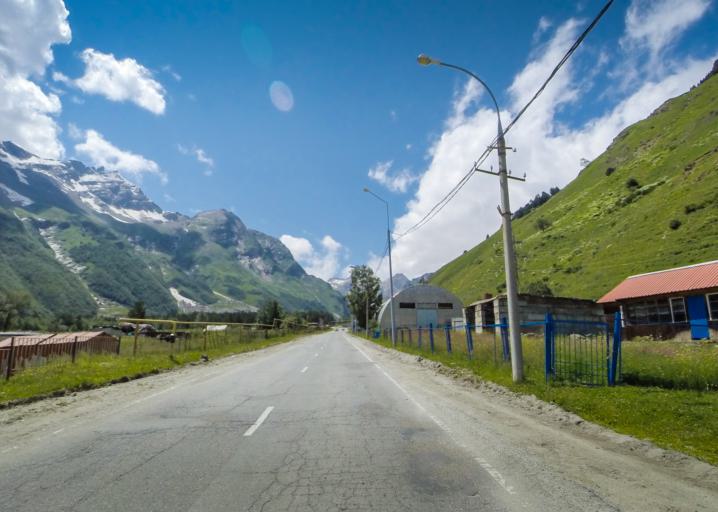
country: RU
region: Kabardino-Balkariya
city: Terskol
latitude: 43.2579
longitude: 42.5100
